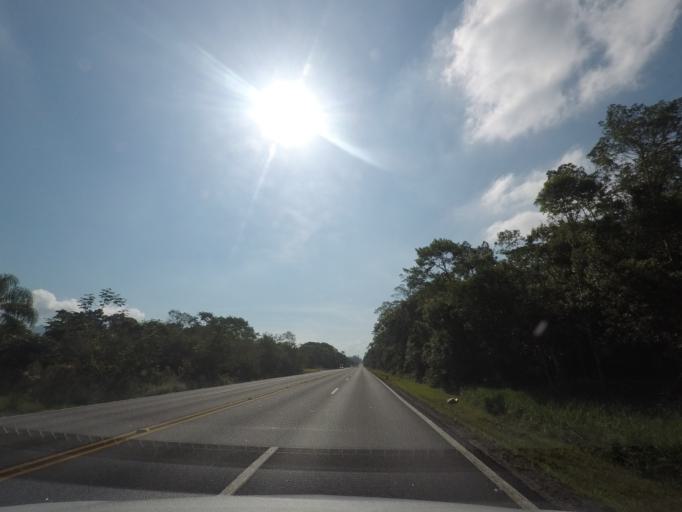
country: BR
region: Parana
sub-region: Pontal Do Parana
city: Pontal do Parana
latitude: -25.6204
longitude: -48.6001
